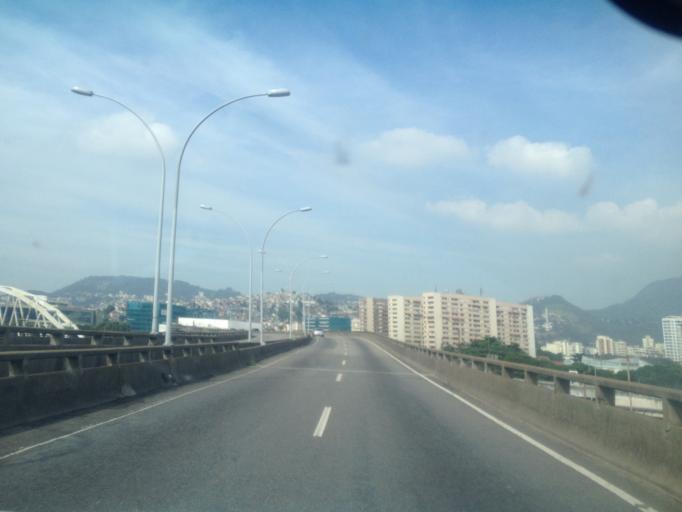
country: BR
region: Rio de Janeiro
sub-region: Rio De Janeiro
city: Rio de Janeiro
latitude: -22.9084
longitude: -43.2123
